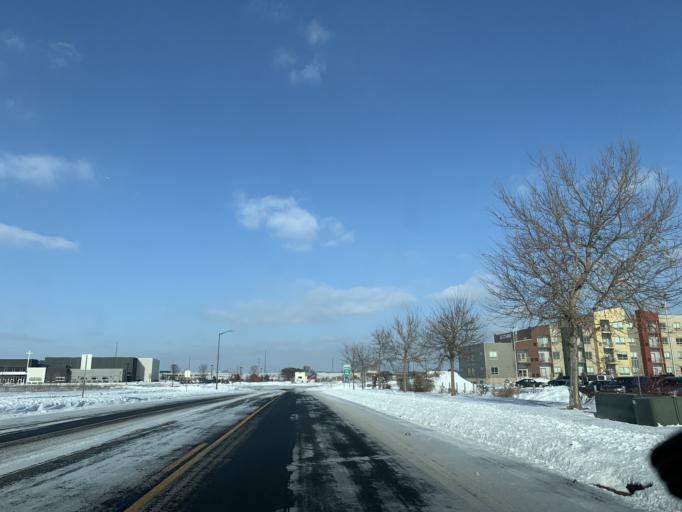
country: US
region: Minnesota
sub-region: Scott County
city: Prior Lake
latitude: 44.7791
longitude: -93.4094
